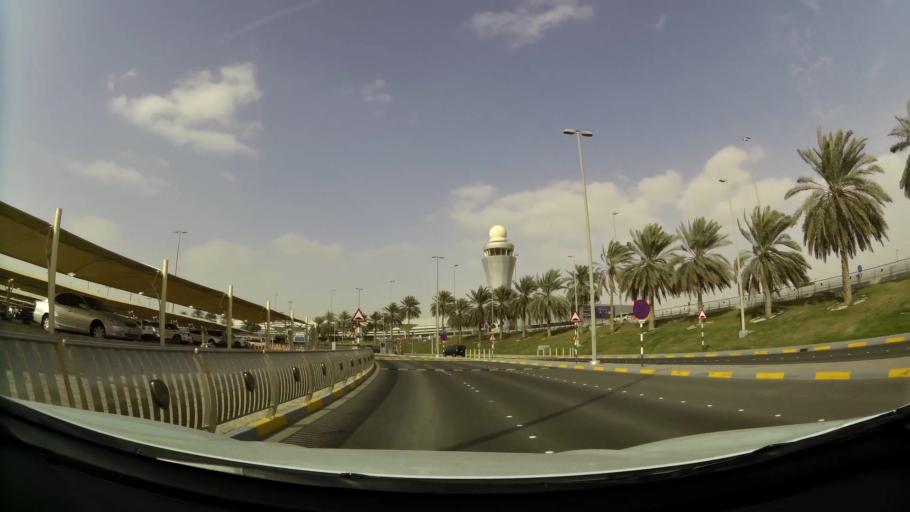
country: AE
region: Abu Dhabi
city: Abu Dhabi
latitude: 24.4248
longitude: 54.6460
